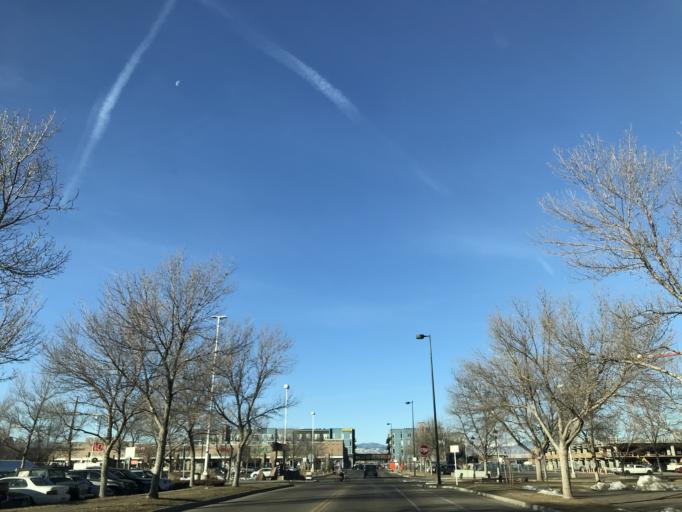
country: US
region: Colorado
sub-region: Denver County
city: Denver
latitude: 39.7093
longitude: -104.9893
